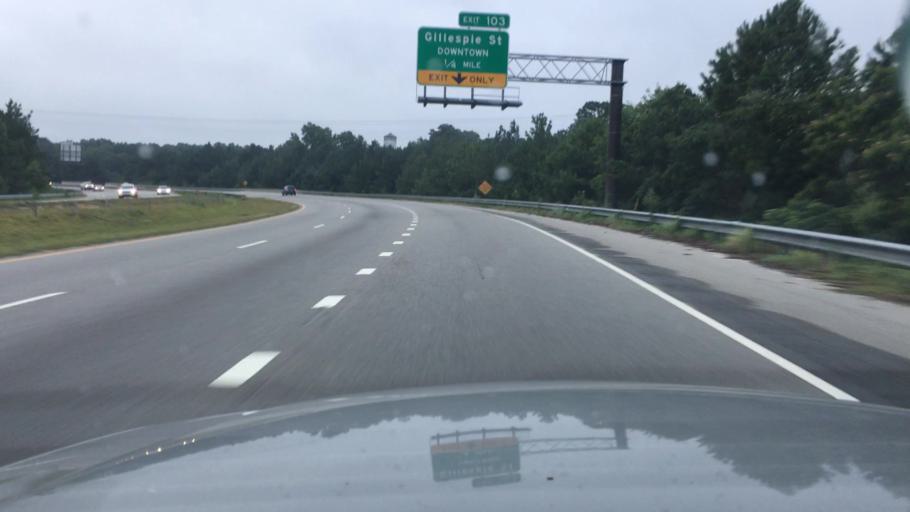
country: US
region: North Carolina
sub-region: Cumberland County
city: Fayetteville
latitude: 35.0409
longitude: -78.8919
